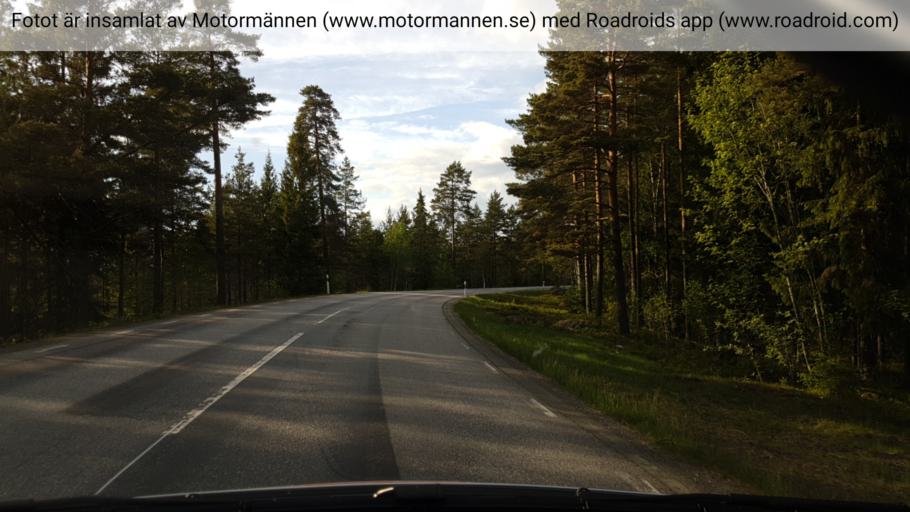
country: SE
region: Vaestmanland
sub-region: Hallstahammars Kommun
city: Hallstahammar
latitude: 59.6503
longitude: 16.1879
